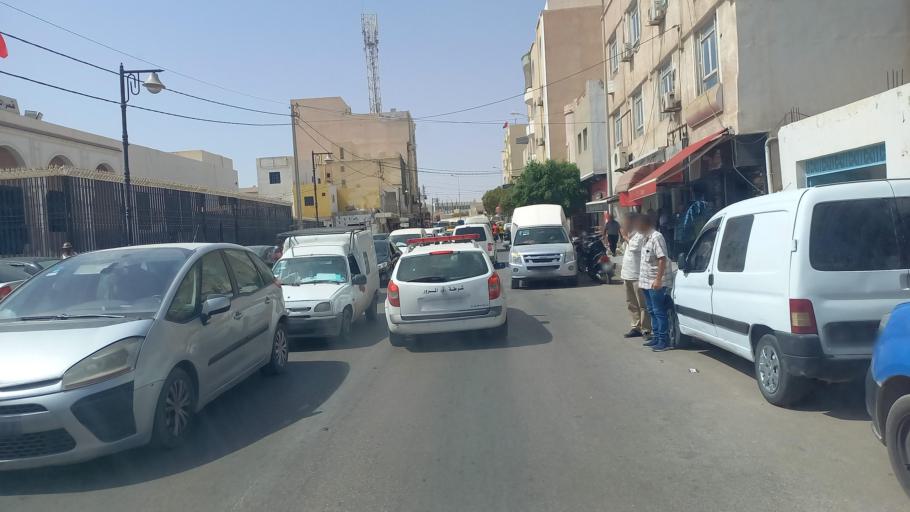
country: TN
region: Madanin
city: Medenine
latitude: 33.3424
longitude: 10.4894
